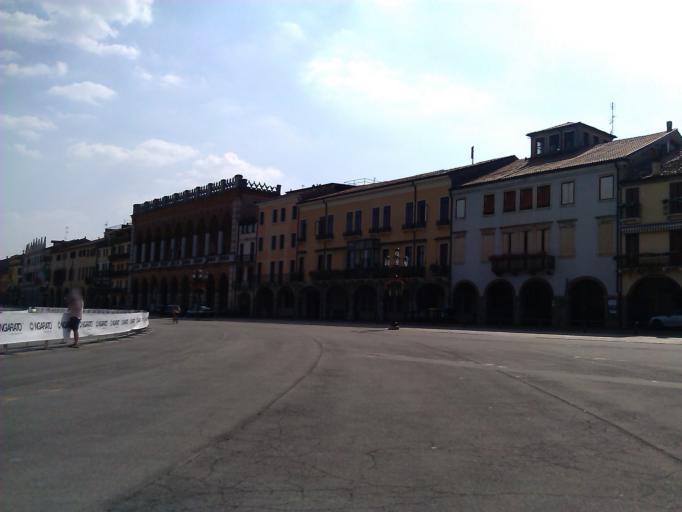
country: IT
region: Veneto
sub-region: Provincia di Padova
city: Padova
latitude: 45.3996
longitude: 11.8760
